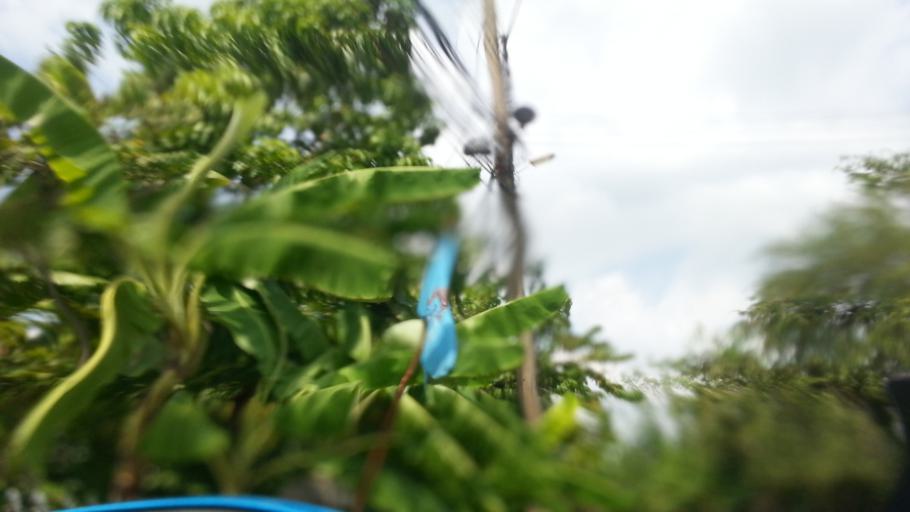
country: TH
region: Pathum Thani
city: Ban Rangsit
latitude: 14.0448
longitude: 100.8308
